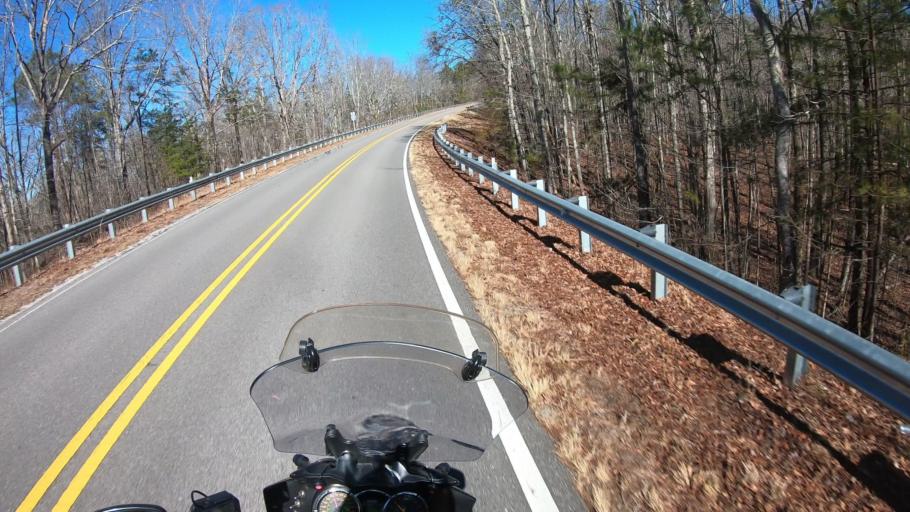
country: US
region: Alabama
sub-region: Calhoun County
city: Choccolocco
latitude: 33.5548
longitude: -85.7136
